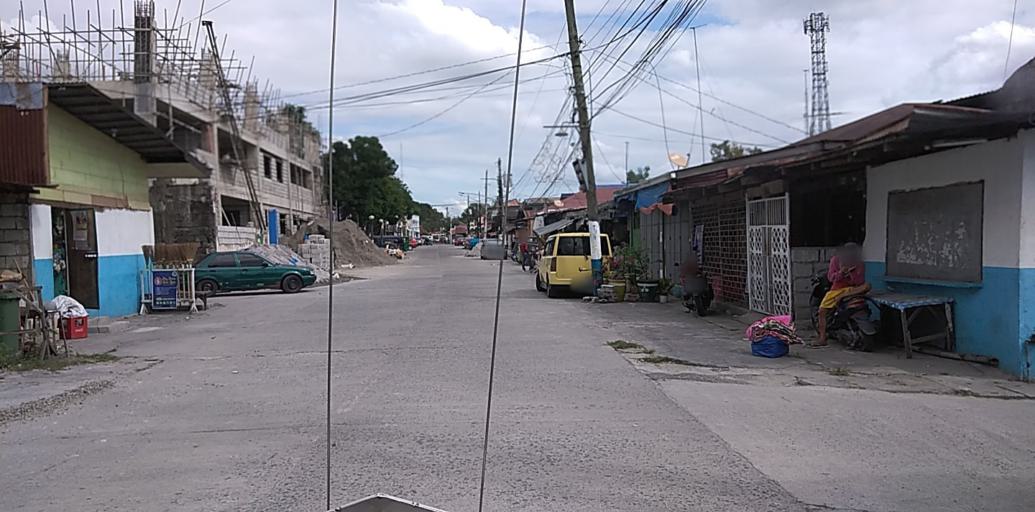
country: PH
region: Central Luzon
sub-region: Province of Pampanga
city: Porac
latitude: 15.0715
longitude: 120.5400
